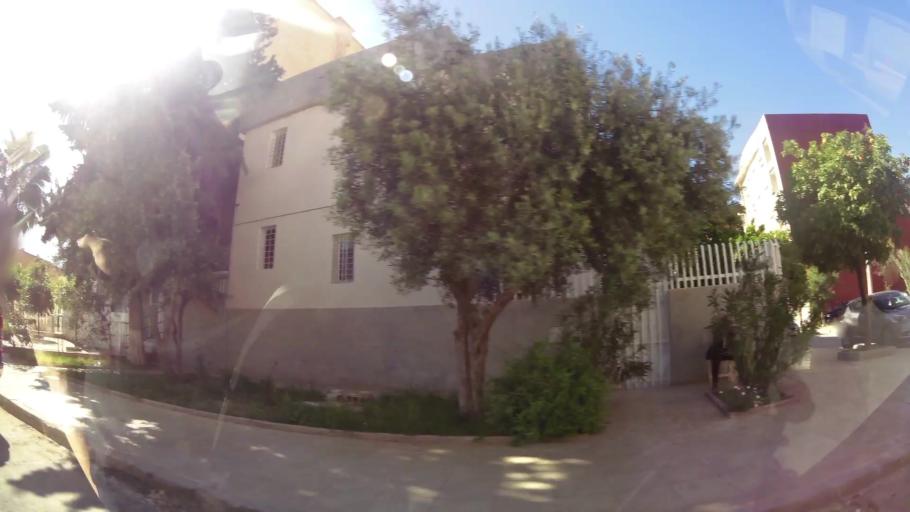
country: MA
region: Oriental
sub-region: Oujda-Angad
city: Oujda
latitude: 34.6599
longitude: -1.8976
